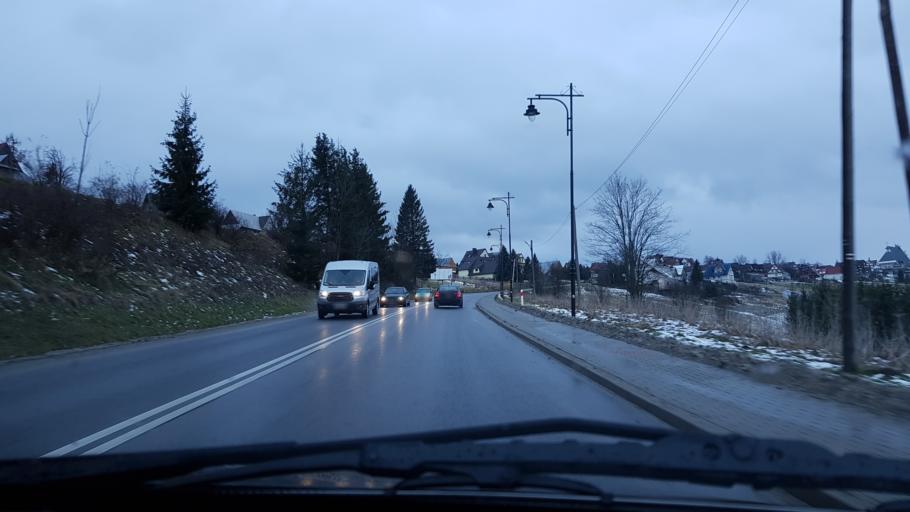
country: PL
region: Lesser Poland Voivodeship
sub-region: Powiat tatrzanski
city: Bukowina Tatrzanska
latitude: 49.3490
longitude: 20.1168
